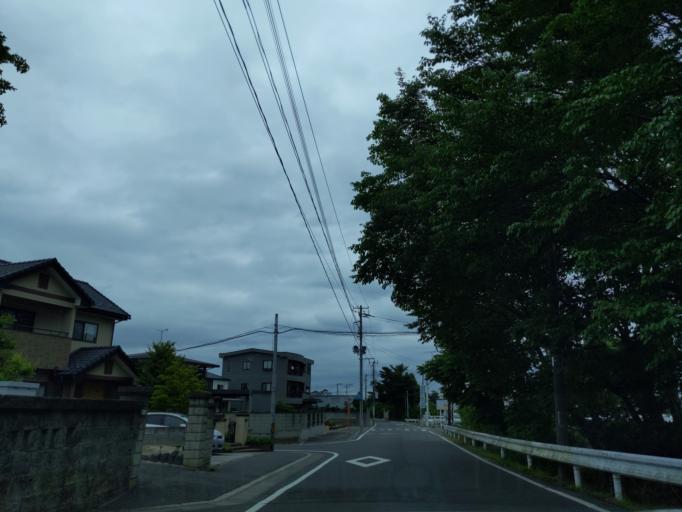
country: JP
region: Fukushima
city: Koriyama
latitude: 37.3467
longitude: 140.3511
